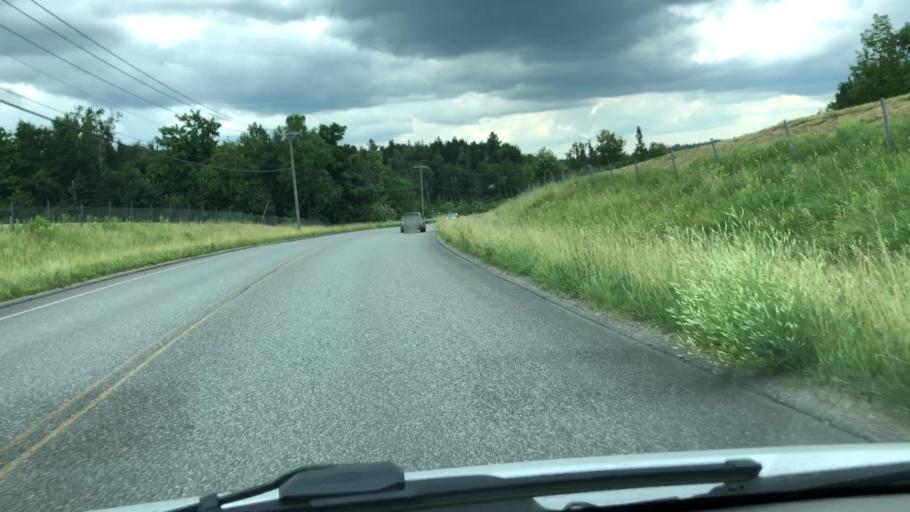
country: US
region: Massachusetts
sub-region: Berkshire County
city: Adams
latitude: 42.5293
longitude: -73.0564
